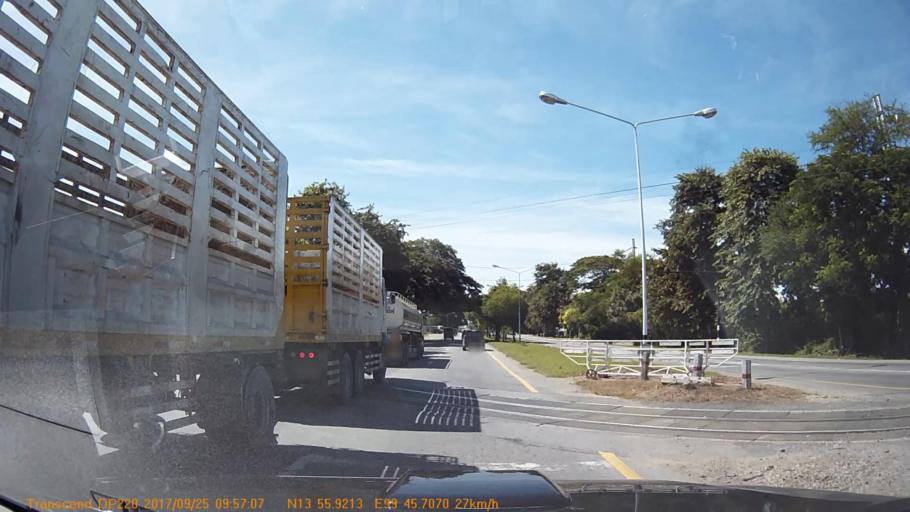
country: TH
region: Kanchanaburi
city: Tha Maka
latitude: 13.9319
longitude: 99.7618
